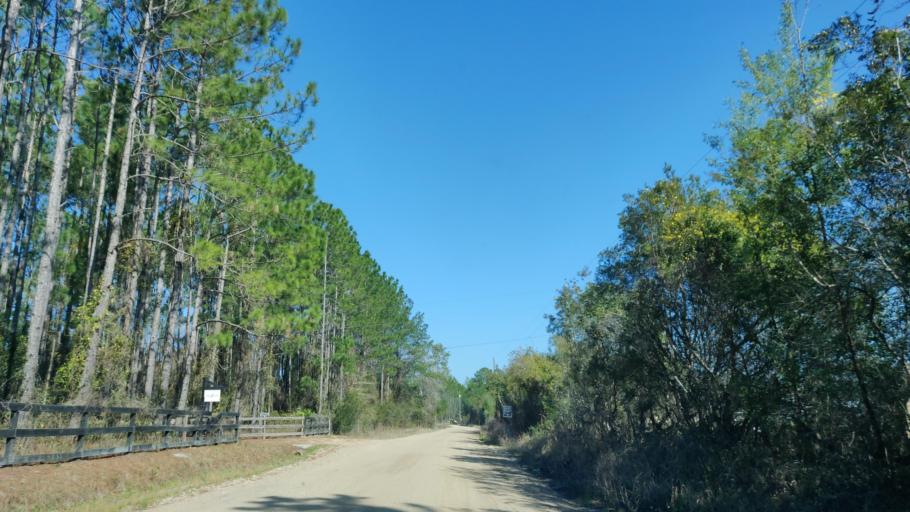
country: US
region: Florida
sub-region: Duval County
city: Baldwin
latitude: 30.1724
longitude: -81.9567
